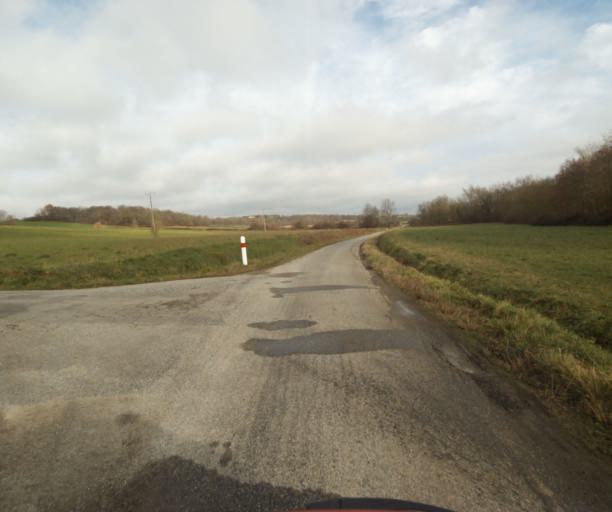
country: FR
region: Midi-Pyrenees
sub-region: Departement de l'Ariege
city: Saverdun
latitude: 43.1793
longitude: 1.5163
